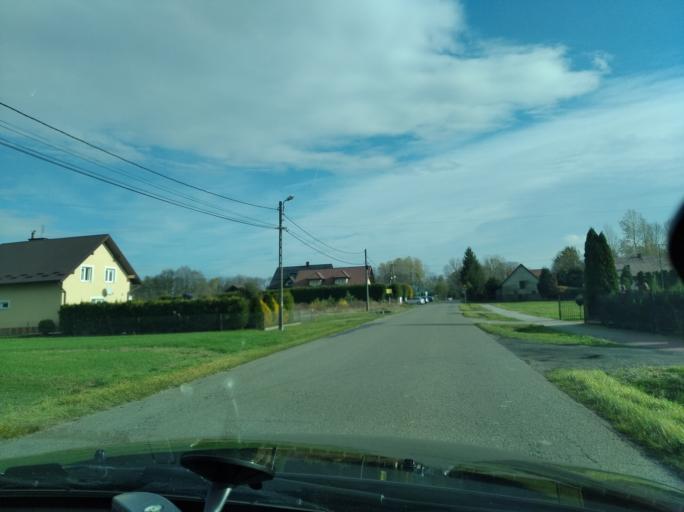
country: PL
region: Subcarpathian Voivodeship
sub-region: Powiat ropczycko-sedziszowski
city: Ostrow
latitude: 50.0958
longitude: 21.6409
